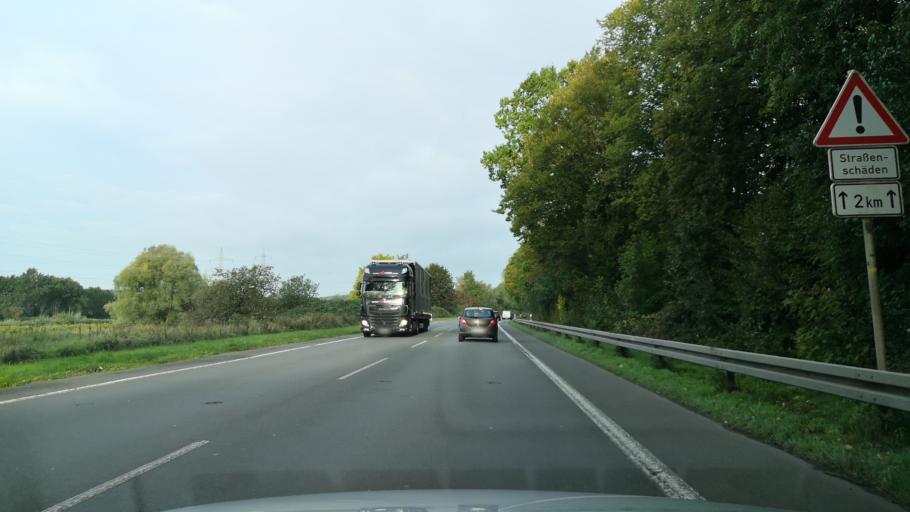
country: DE
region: North Rhine-Westphalia
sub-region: Regierungsbezirk Arnsberg
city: Hagen
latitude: 51.3936
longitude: 7.5139
